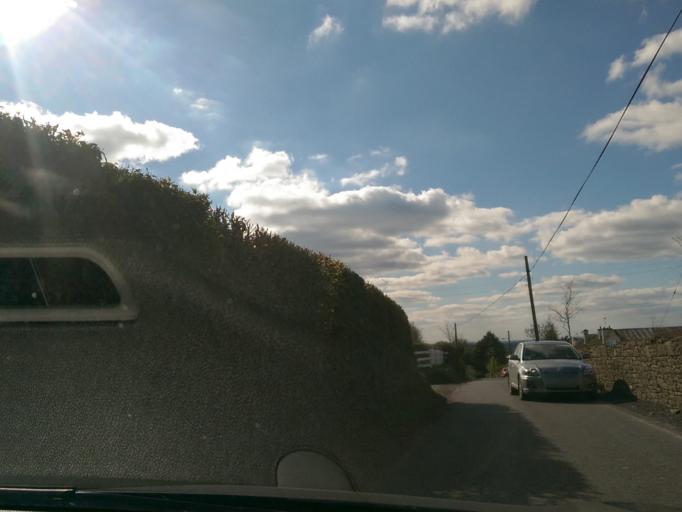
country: IE
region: Munster
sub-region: North Tipperary
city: Roscrea
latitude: 53.0967
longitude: -7.7073
